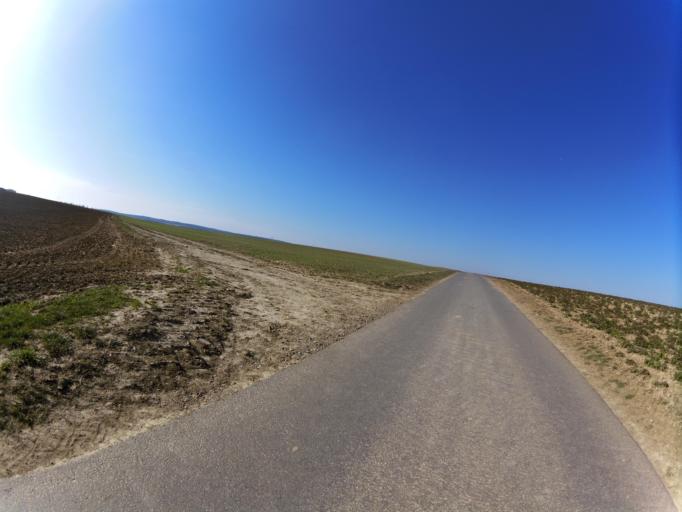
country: DE
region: Bavaria
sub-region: Regierungsbezirk Unterfranken
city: Oberpleichfeld
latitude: 49.8748
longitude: 10.0661
